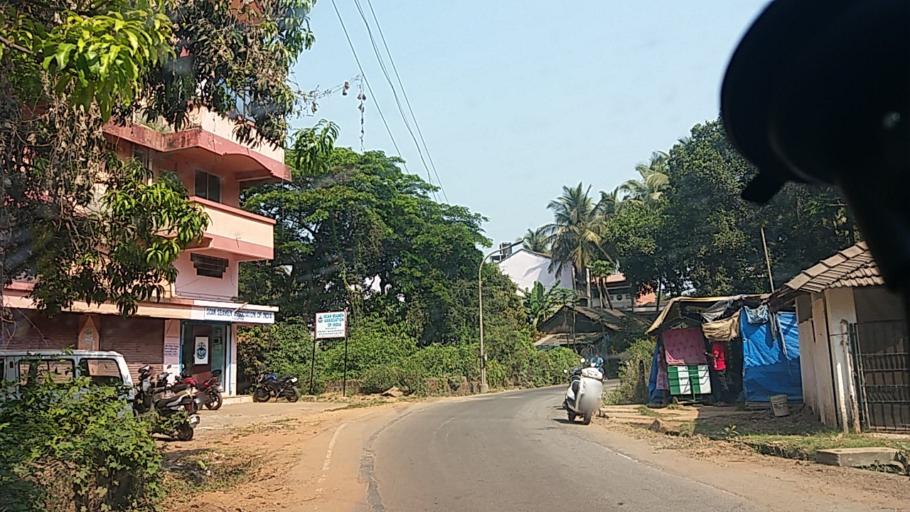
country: IN
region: Goa
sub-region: South Goa
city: Madgaon
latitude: 15.2878
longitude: 73.9530
